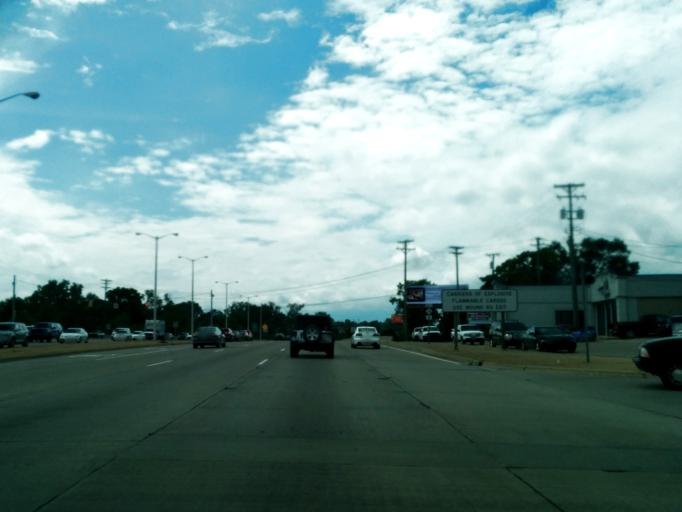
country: US
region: Michigan
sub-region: Macomb County
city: Utica
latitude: 42.6256
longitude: -83.0328
